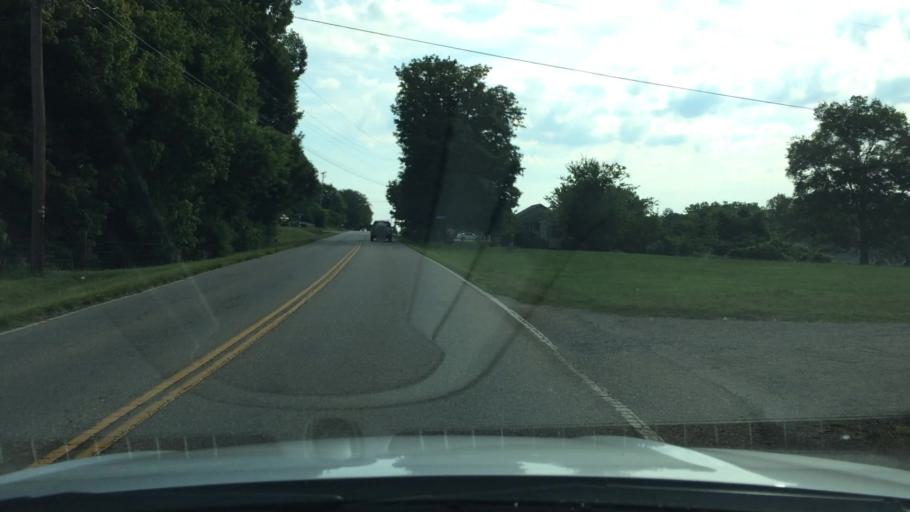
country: US
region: Tennessee
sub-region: Sevier County
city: Seymour
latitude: 35.8944
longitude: -83.7154
